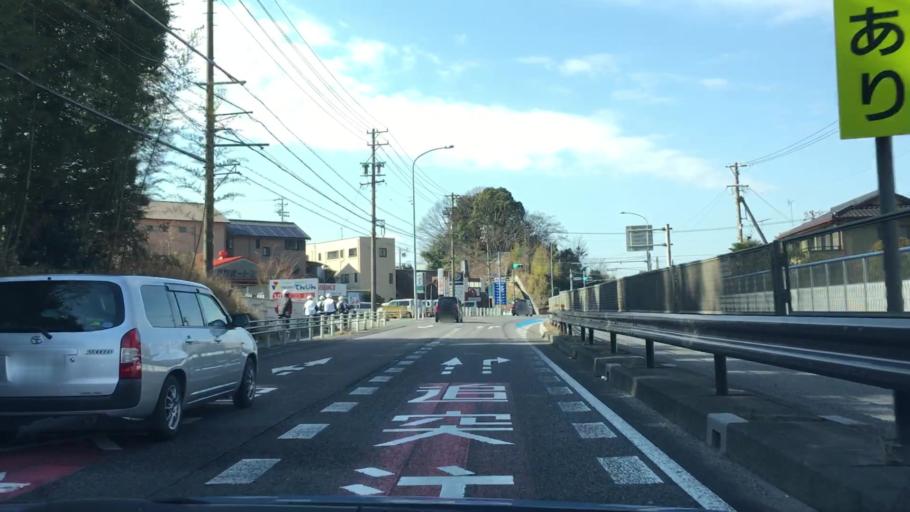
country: JP
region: Aichi
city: Gamagori
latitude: 34.8983
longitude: 137.2450
